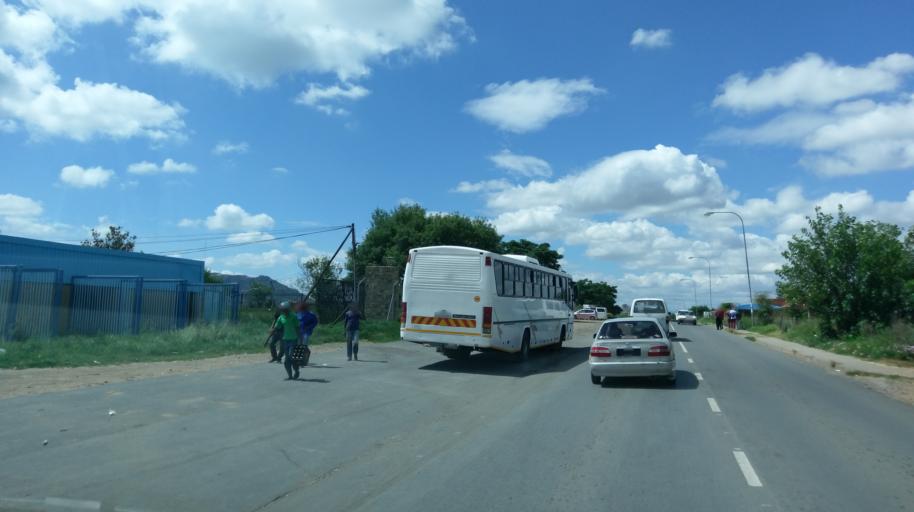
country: LS
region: Maseru
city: Maseru
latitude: -29.3122
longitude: 27.5007
